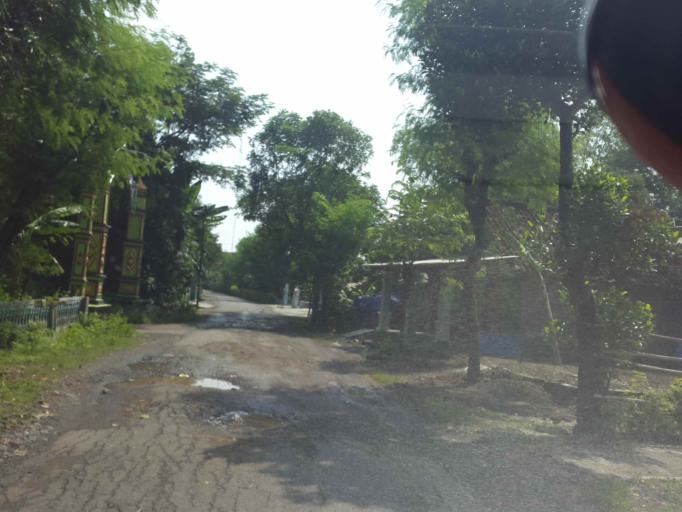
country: ID
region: Central Java
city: Sragen
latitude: -7.4437
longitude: 110.9502
